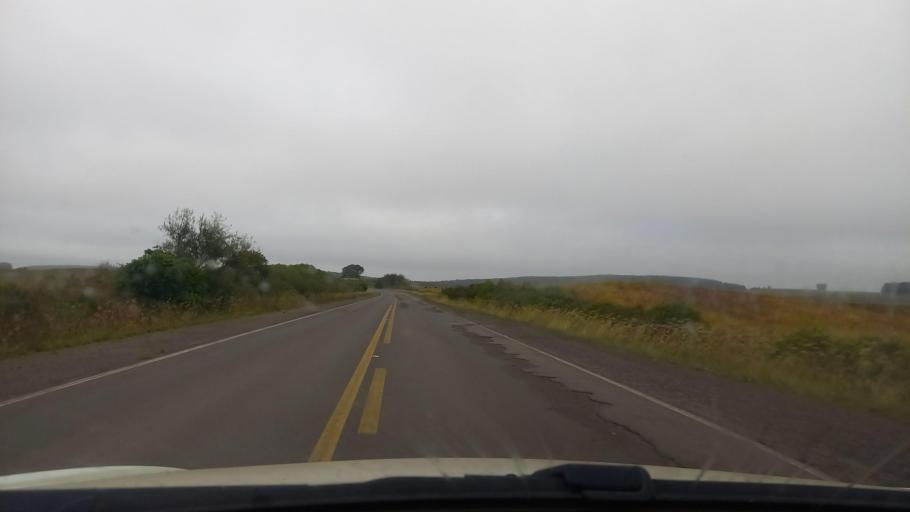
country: BR
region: Rio Grande do Sul
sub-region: Rosario Do Sul
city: Rosario do Sul
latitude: -30.1416
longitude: -54.6691
